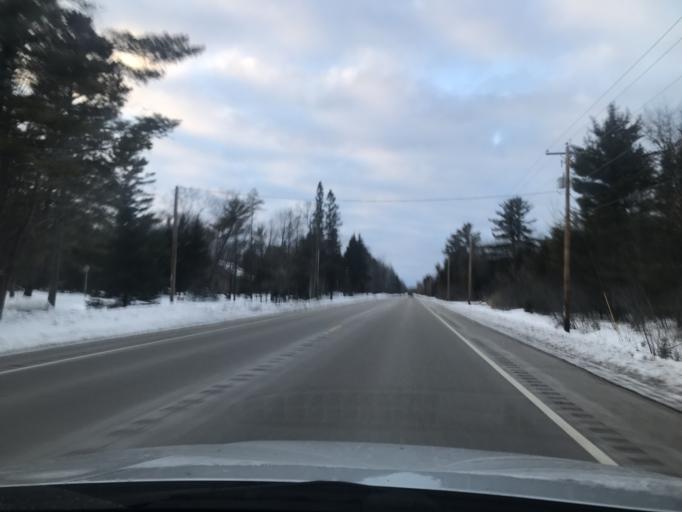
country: US
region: Wisconsin
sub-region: Marinette County
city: Marinette
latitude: 45.1441
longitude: -87.6962
